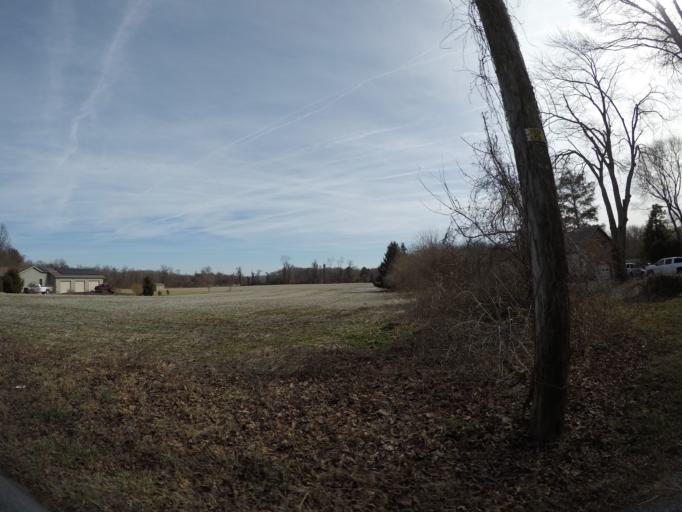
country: US
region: Maryland
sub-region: Harford County
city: Aberdeen
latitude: 39.6564
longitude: -76.2221
